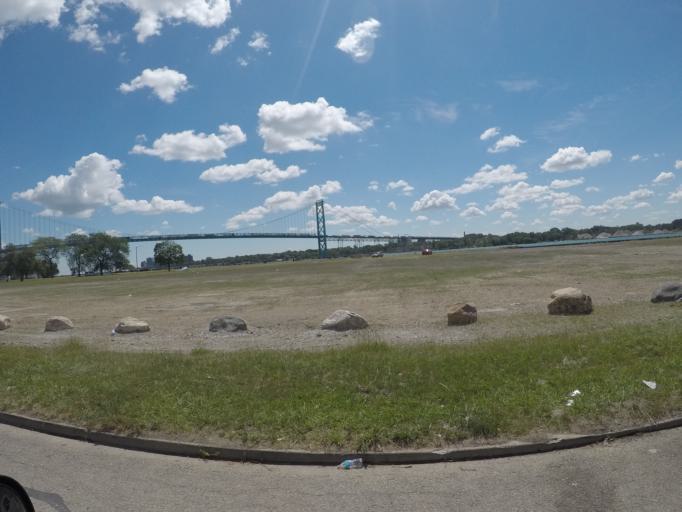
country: US
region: Michigan
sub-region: Wayne County
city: Detroit
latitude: 42.3111
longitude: -83.0822
